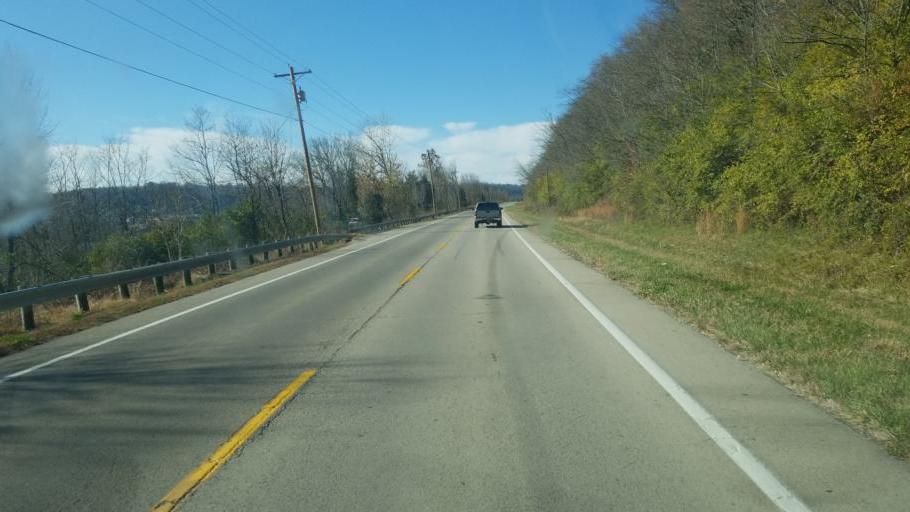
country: US
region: Kentucky
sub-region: Mason County
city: Maysville
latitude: 38.6495
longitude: -83.7396
